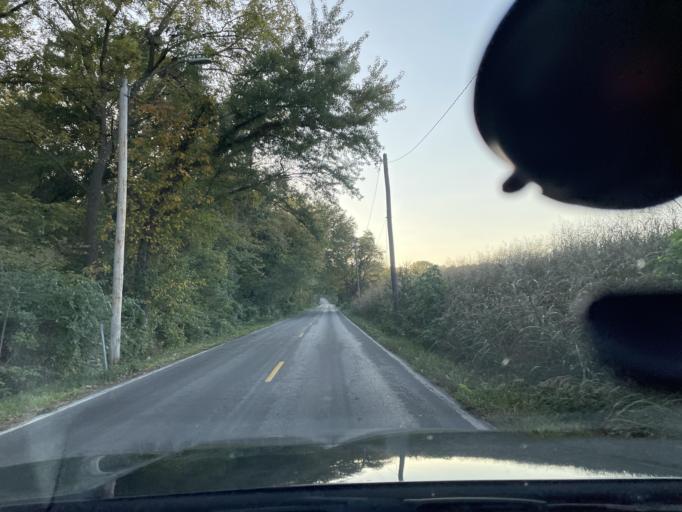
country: US
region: Missouri
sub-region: Buchanan County
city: Saint Joseph
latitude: 39.7994
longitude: -94.8338
